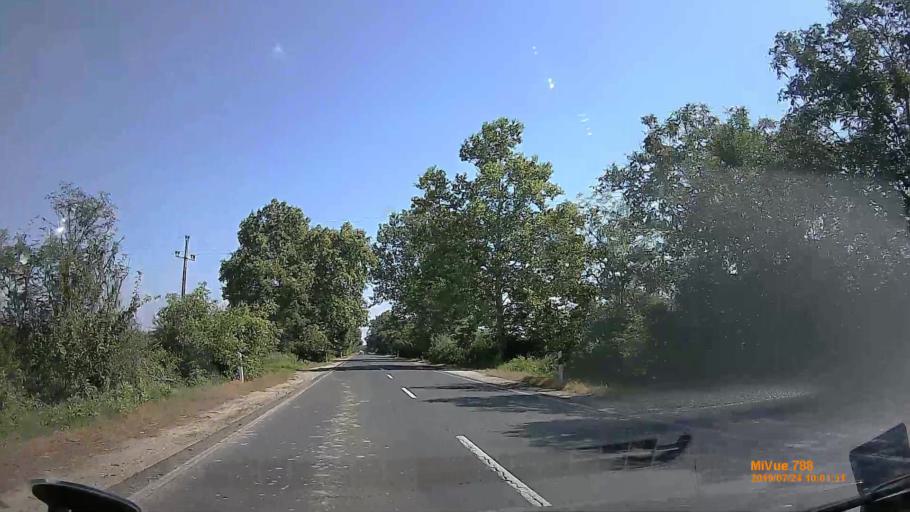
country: HU
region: Szabolcs-Szatmar-Bereg
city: Vasarosnameny
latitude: 48.1007
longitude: 22.2952
